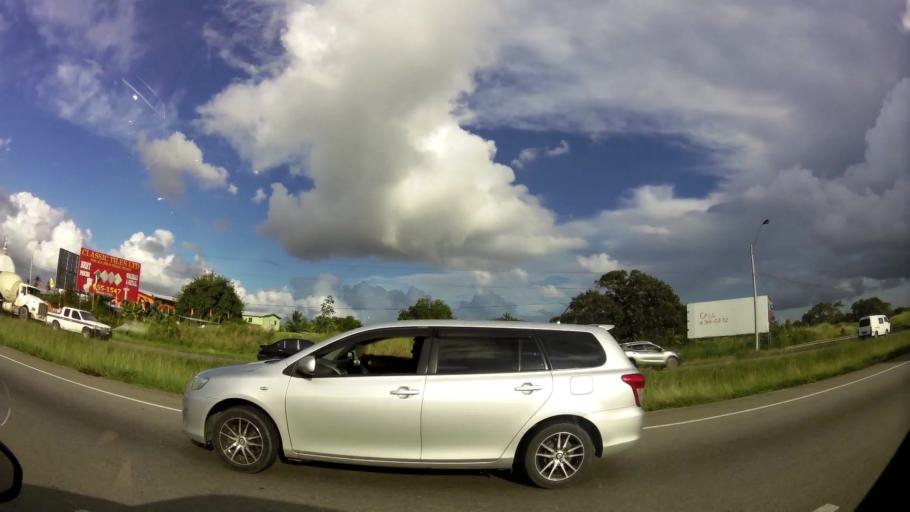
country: TT
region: Chaguanas
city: Chaguanas
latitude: 10.4792
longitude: -61.4052
